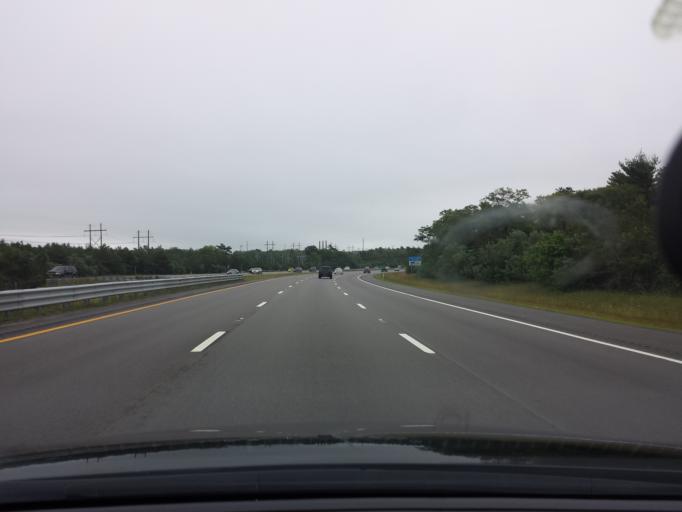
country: US
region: Massachusetts
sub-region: Barnstable County
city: Bourne
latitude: 41.7801
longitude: -70.5948
